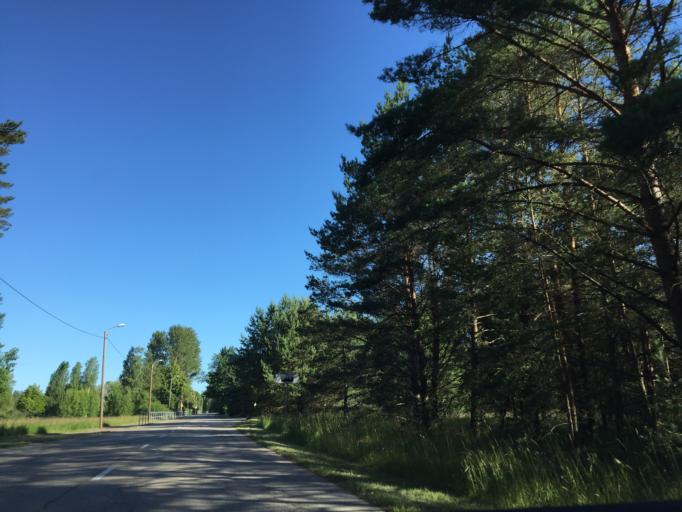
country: LV
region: Ventspils
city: Ventspils
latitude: 57.4349
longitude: 21.6249
